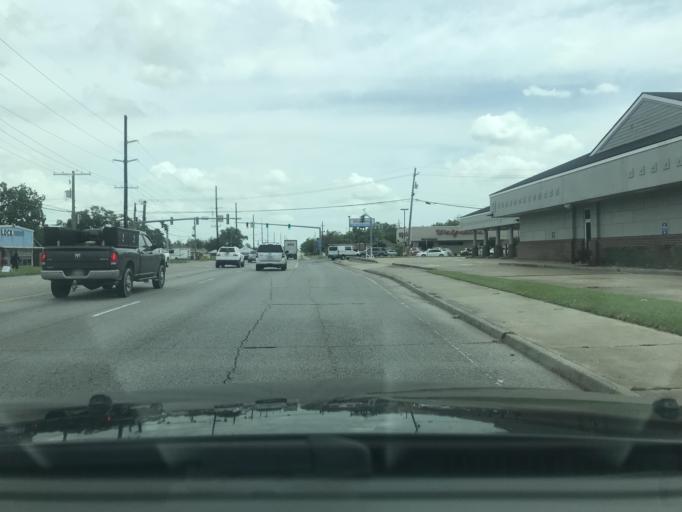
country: US
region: Louisiana
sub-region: Calcasieu Parish
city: Lake Charles
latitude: 30.2139
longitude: -93.1802
